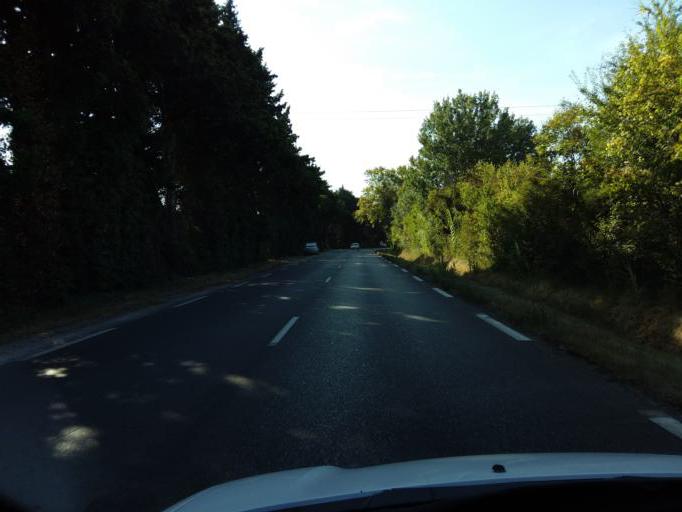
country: FR
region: Provence-Alpes-Cote d'Azur
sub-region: Departement du Vaucluse
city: L'Isle-sur-la-Sorgue
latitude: 43.9210
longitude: 5.0231
